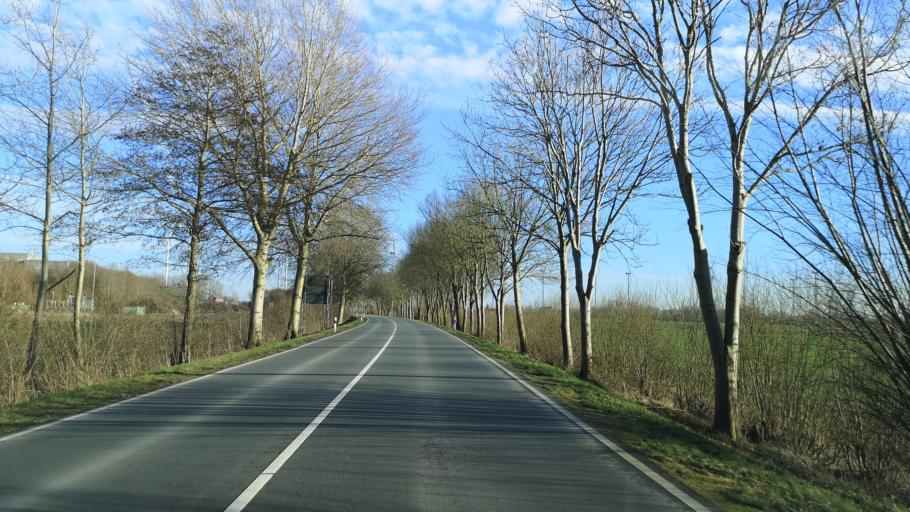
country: DE
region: Schleswig-Holstein
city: Lagerdorf
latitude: 53.8713
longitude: 9.5781
